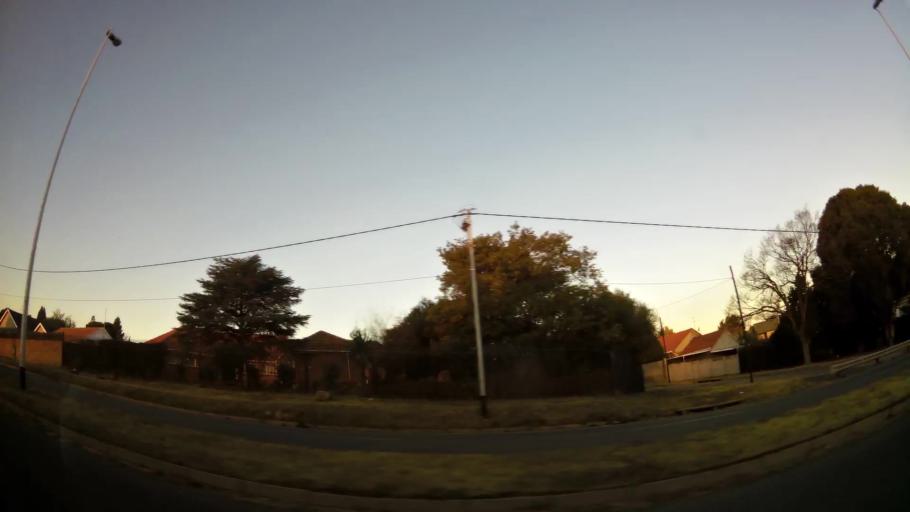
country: ZA
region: Gauteng
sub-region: City of Johannesburg Metropolitan Municipality
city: Roodepoort
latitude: -26.1544
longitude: 27.9060
